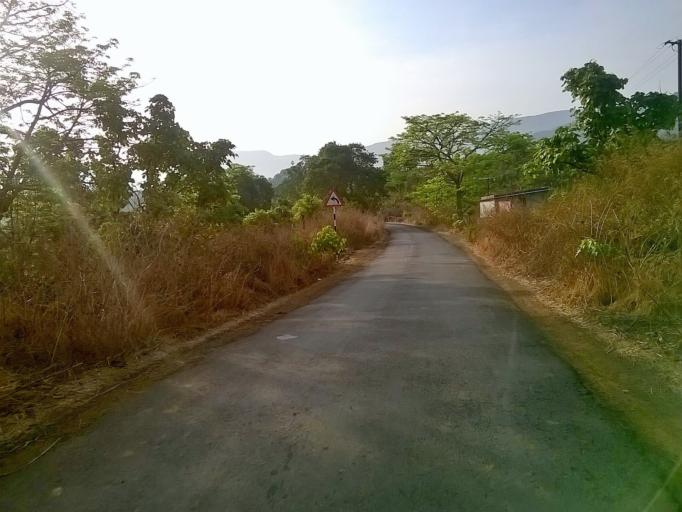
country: IN
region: Maharashtra
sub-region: Raigarh
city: Matheran
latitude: 19.0266
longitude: 73.2296
